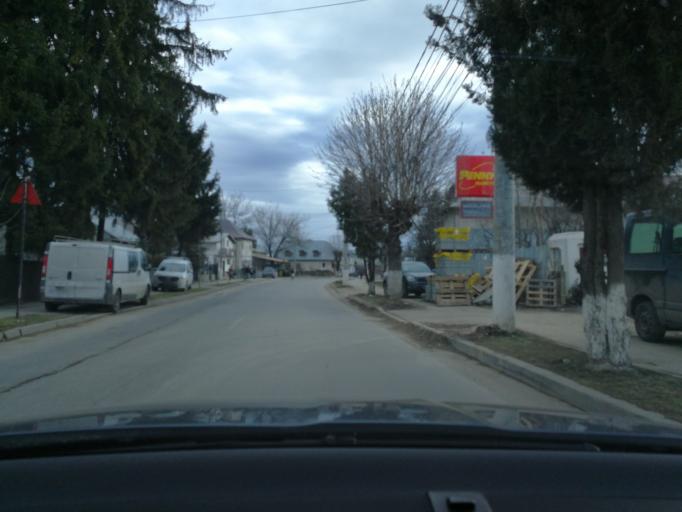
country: RO
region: Prahova
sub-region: Oras Breaza
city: Breaza de Jos
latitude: 45.1757
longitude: 25.6714
